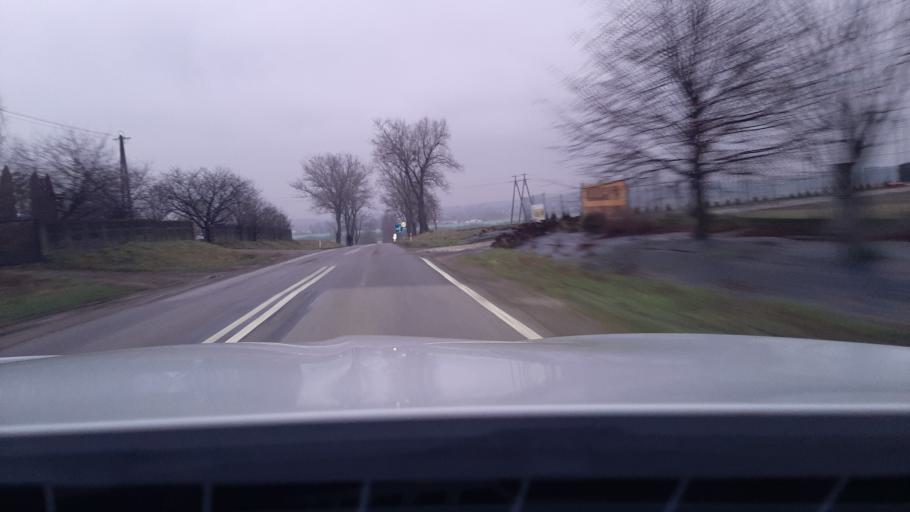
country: PL
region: Lublin Voivodeship
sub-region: Powiat lubelski
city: Garbow
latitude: 51.3459
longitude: 22.3645
